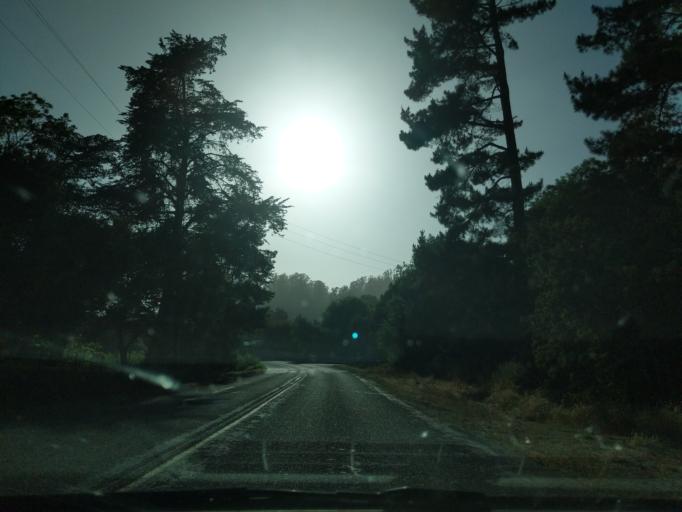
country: US
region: California
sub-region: Monterey County
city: Prunedale
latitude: 36.8253
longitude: -121.6616
